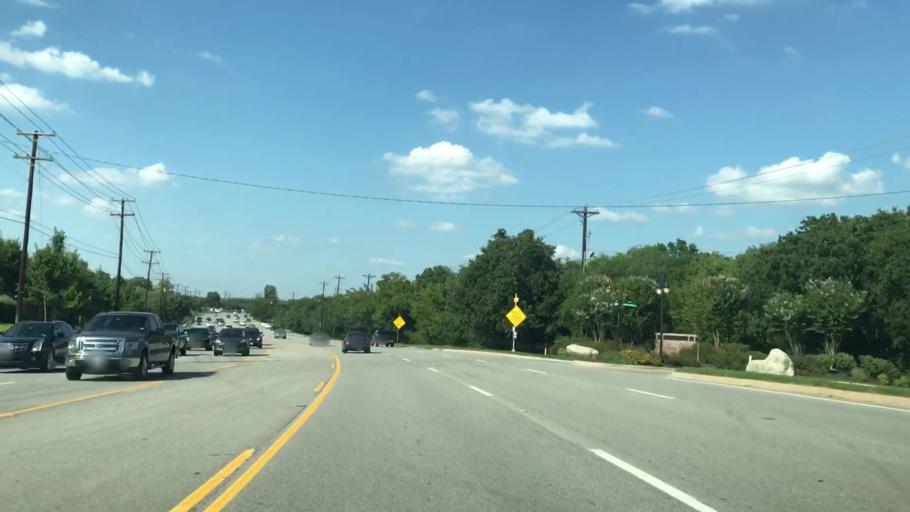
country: US
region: Texas
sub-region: Tarrant County
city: Colleyville
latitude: 32.9157
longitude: -97.1864
